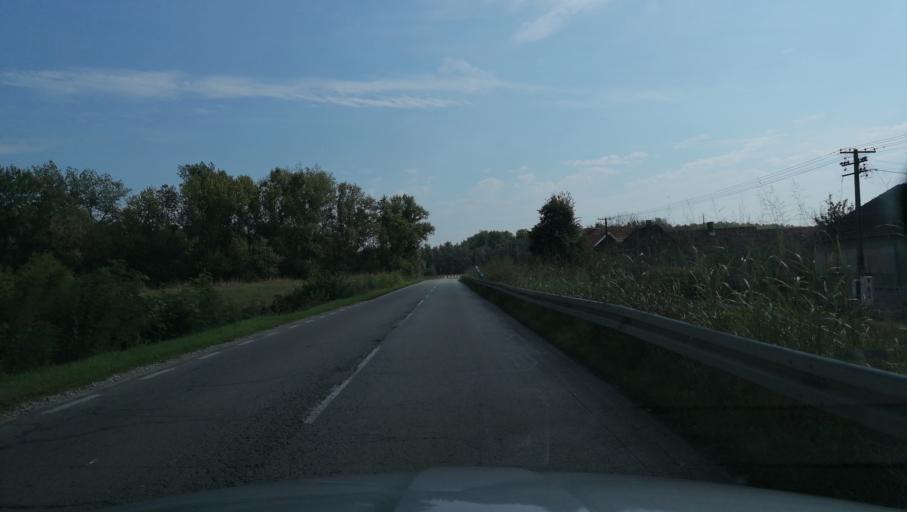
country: RS
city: Bosut
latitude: 44.9407
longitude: 19.3668
